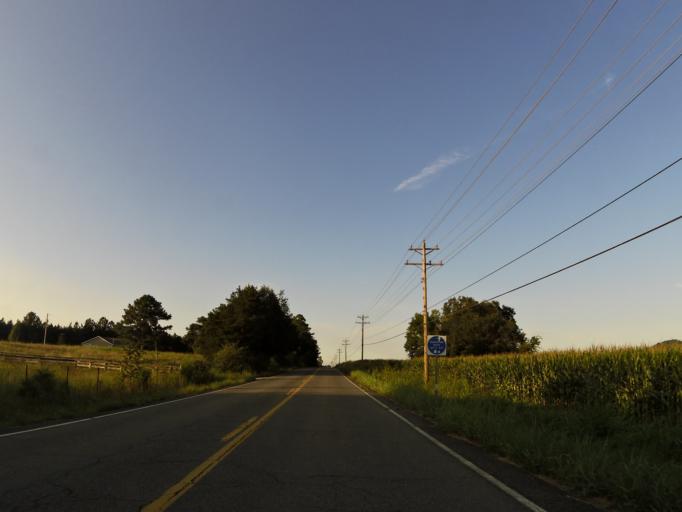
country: US
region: Tennessee
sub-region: Roane County
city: Rockwood
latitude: 35.6815
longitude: -84.6676
